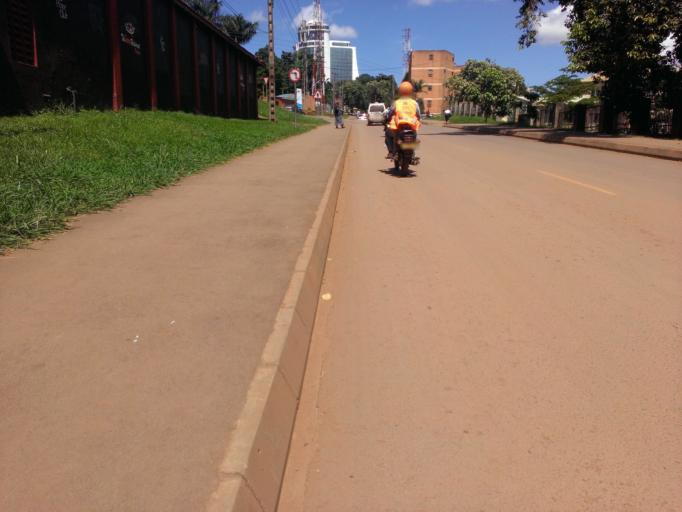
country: UG
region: Central Region
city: Kampala Central Division
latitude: 0.3276
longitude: 32.5754
